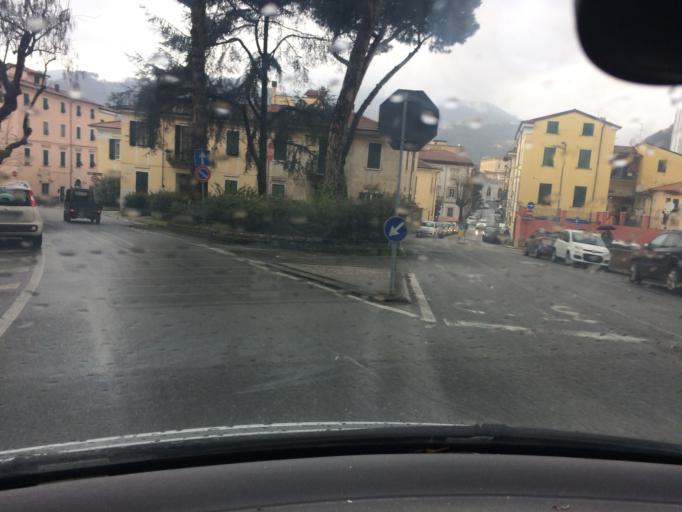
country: IT
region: Tuscany
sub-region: Provincia di Massa-Carrara
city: Carrara
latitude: 44.0755
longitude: 10.1040
